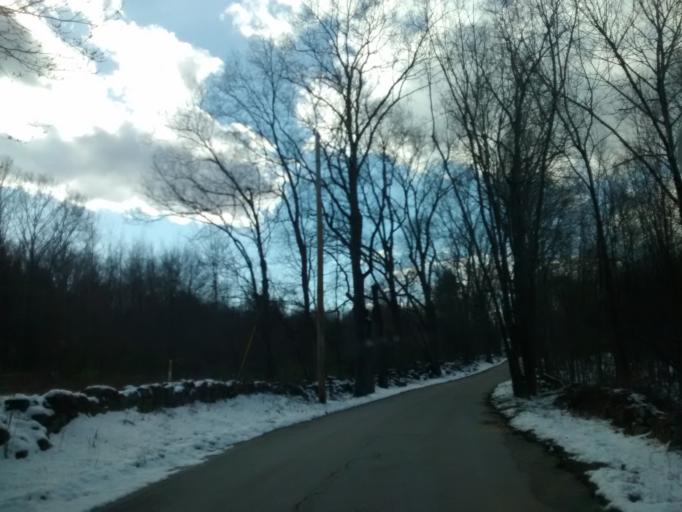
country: US
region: Massachusetts
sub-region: Worcester County
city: East Douglas
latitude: 42.0433
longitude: -71.6862
